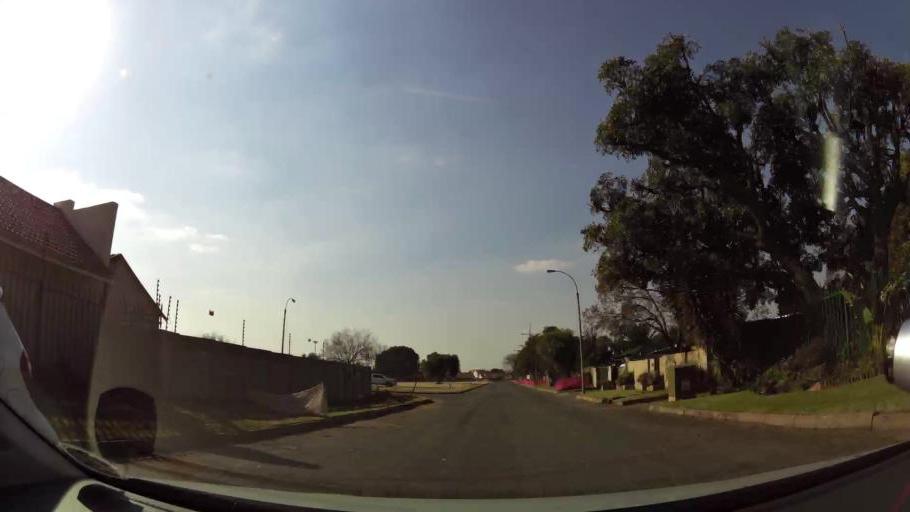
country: ZA
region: Gauteng
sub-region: City of Johannesburg Metropolitan Municipality
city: Modderfontein
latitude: -26.0935
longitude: 28.2030
